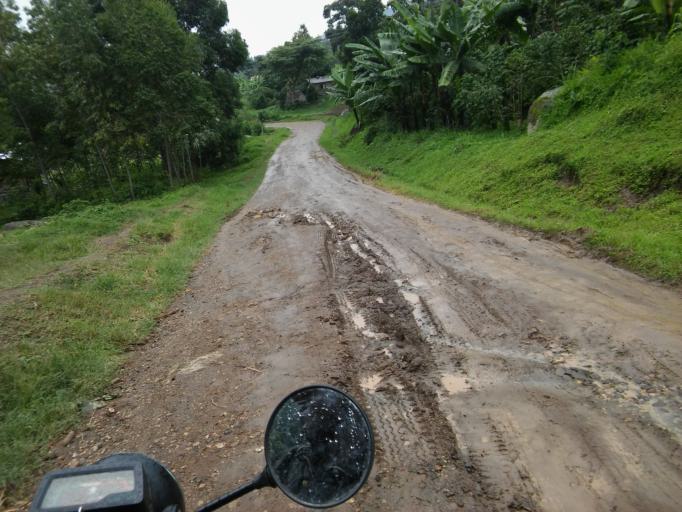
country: UG
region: Eastern Region
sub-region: Bududa District
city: Bududa
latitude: 1.0079
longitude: 34.2373
